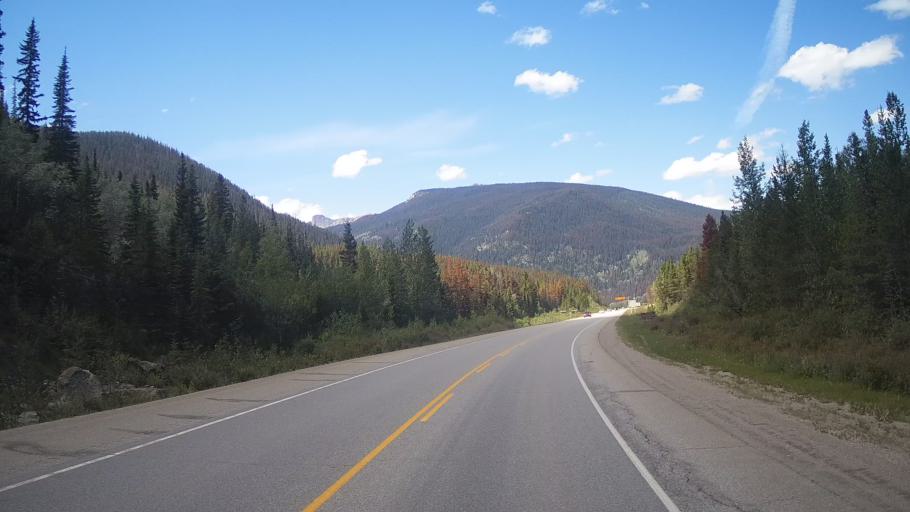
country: CA
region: Alberta
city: Jasper Park Lodge
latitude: 52.8822
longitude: -118.4536
